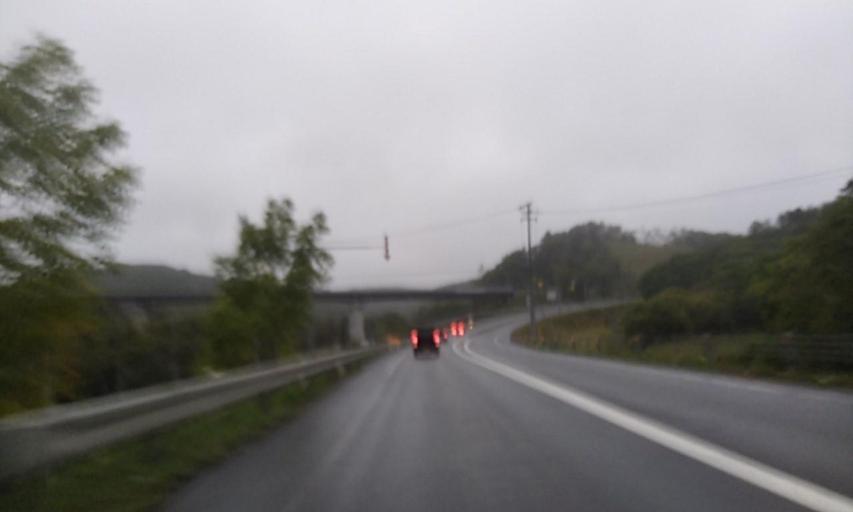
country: JP
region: Hokkaido
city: Kushiro
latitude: 43.0012
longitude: 144.5014
